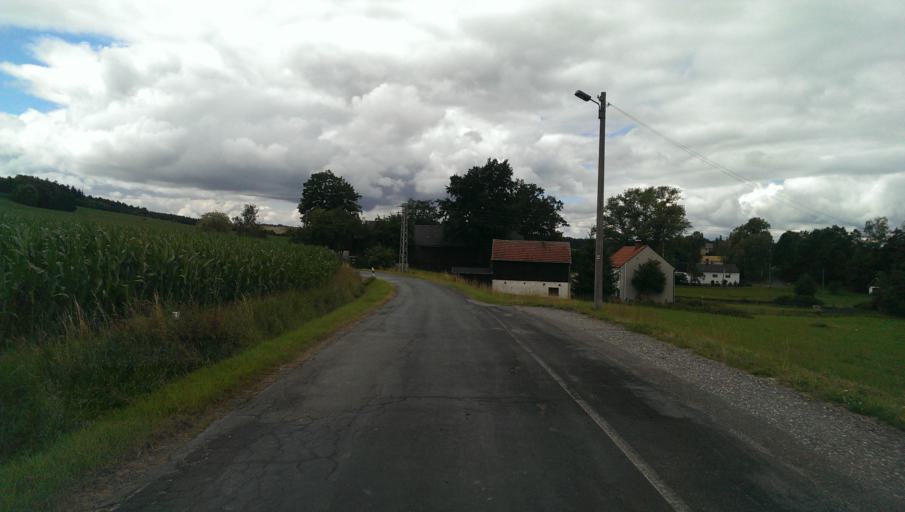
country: DE
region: Saxony
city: Pausa
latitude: 50.5979
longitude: 11.9818
